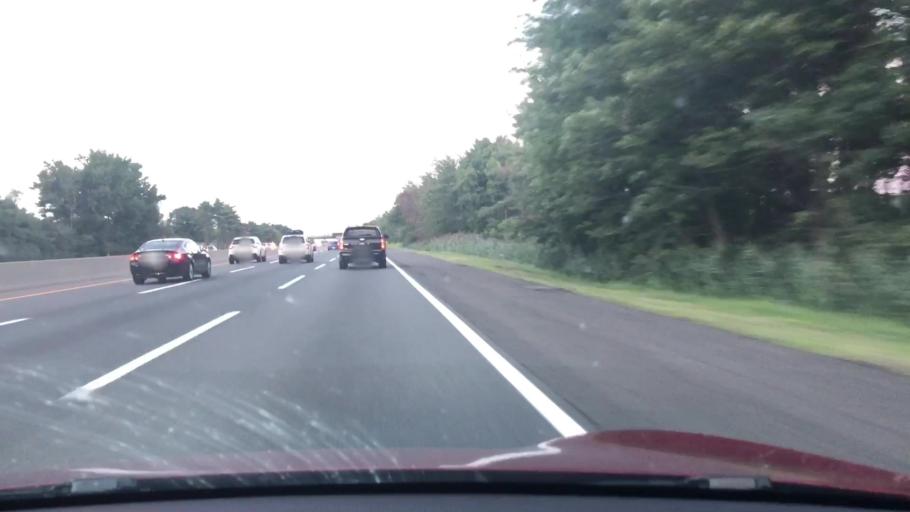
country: US
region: New Jersey
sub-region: Burlington County
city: Mount Laurel
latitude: 39.9628
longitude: -74.9124
